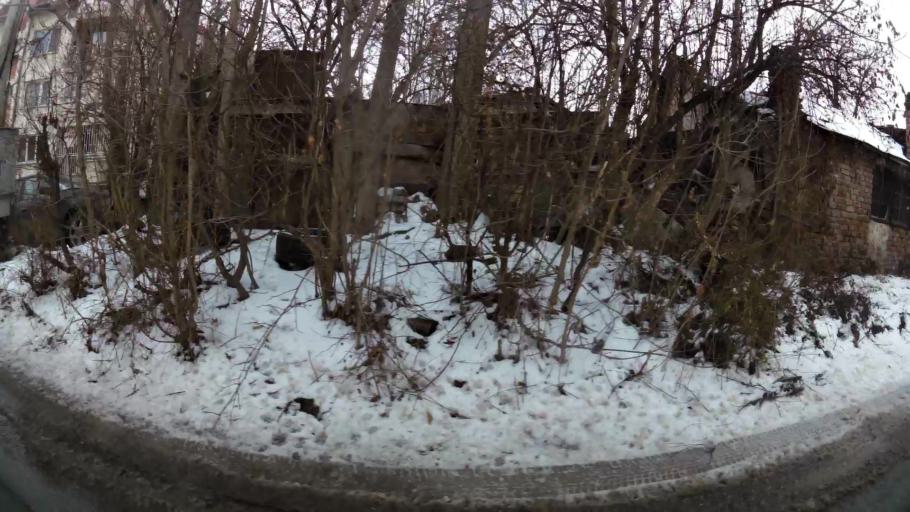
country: BG
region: Sofia-Capital
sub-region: Stolichna Obshtina
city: Sofia
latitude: 42.6994
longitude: 23.3553
